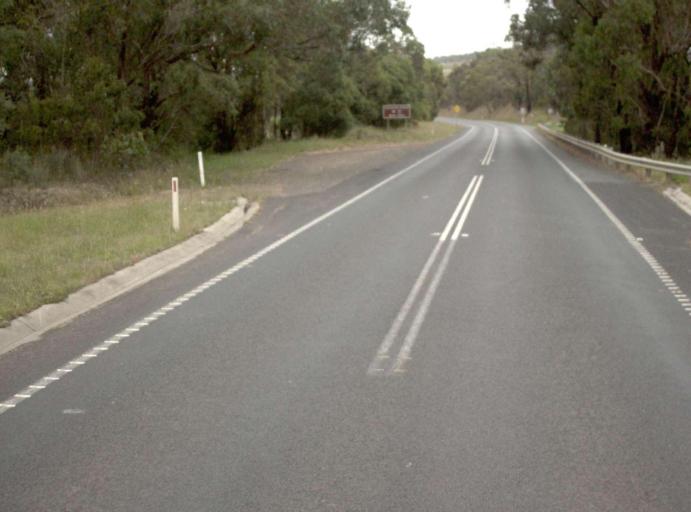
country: AU
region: Victoria
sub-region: Yarra Ranges
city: Yarra Glen
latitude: -37.5737
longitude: 145.4138
